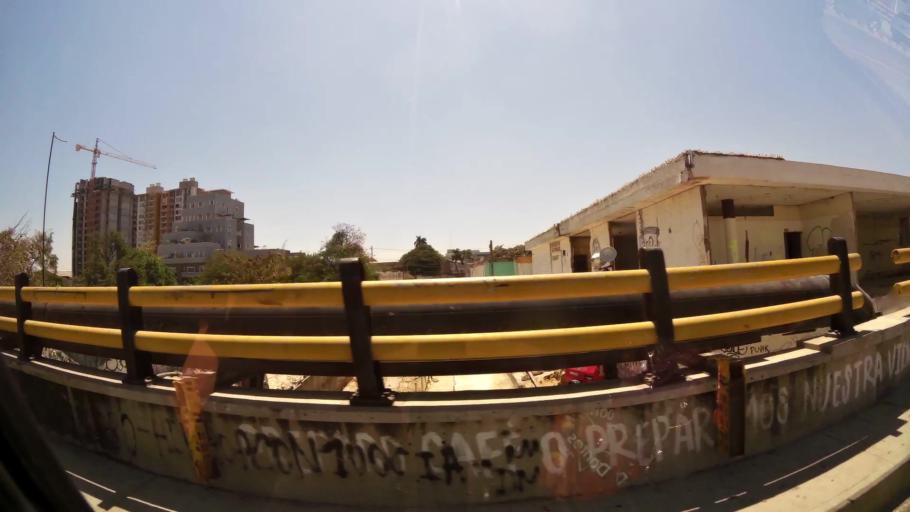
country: CO
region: Atlantico
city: Barranquilla
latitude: 10.9877
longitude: -74.7865
